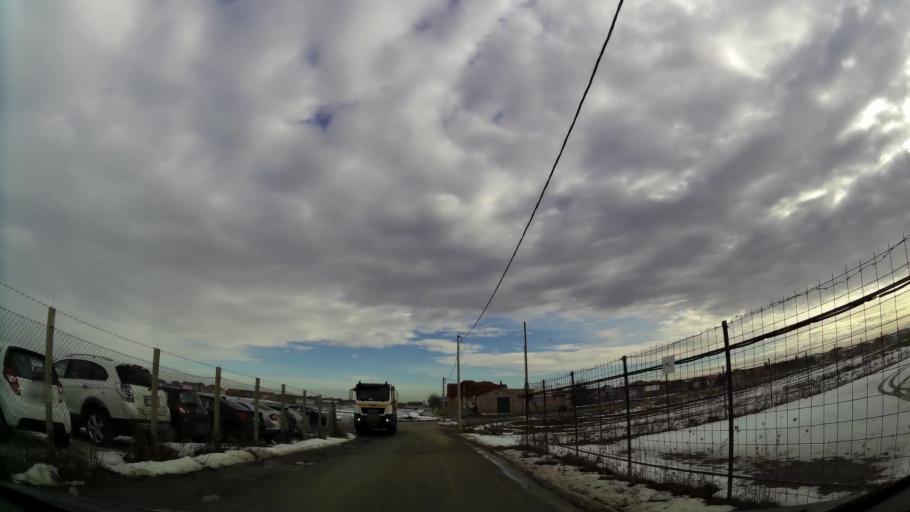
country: RS
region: Central Serbia
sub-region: Belgrade
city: Surcin
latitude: 44.8016
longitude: 20.3160
